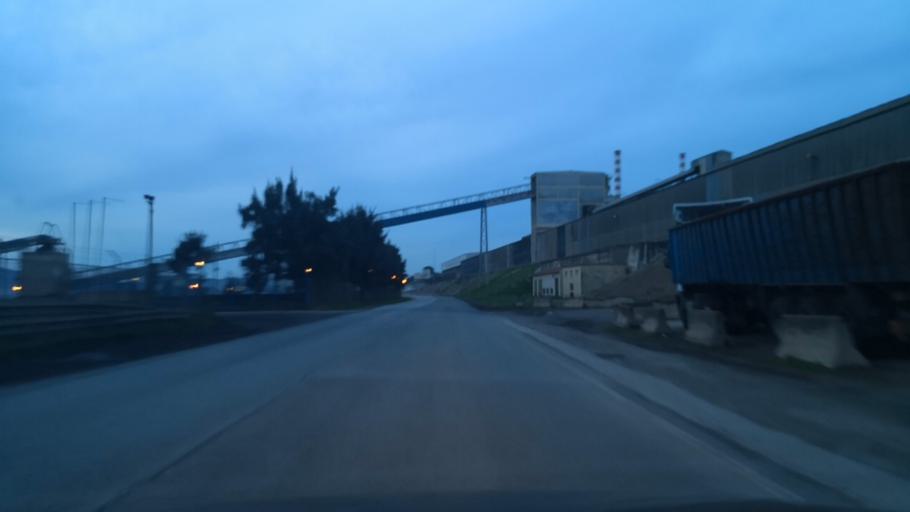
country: PT
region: Setubal
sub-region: Setubal
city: Setubal
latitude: 38.5003
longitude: -8.8404
